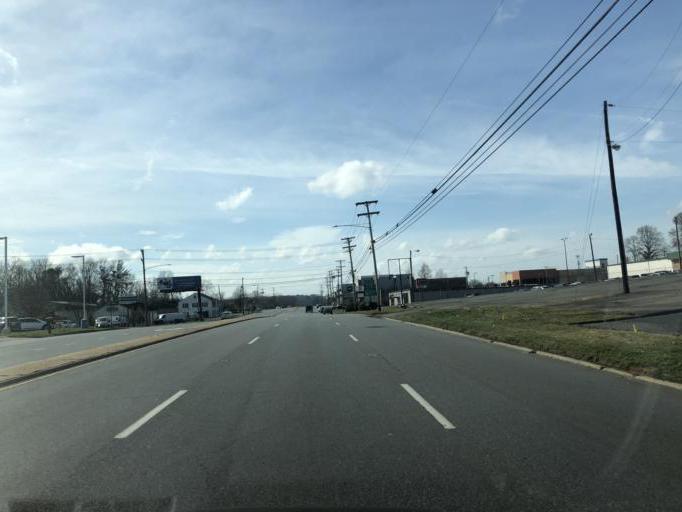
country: US
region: North Carolina
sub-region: Gaston County
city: Lowell
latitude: 35.2568
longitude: -81.1072
